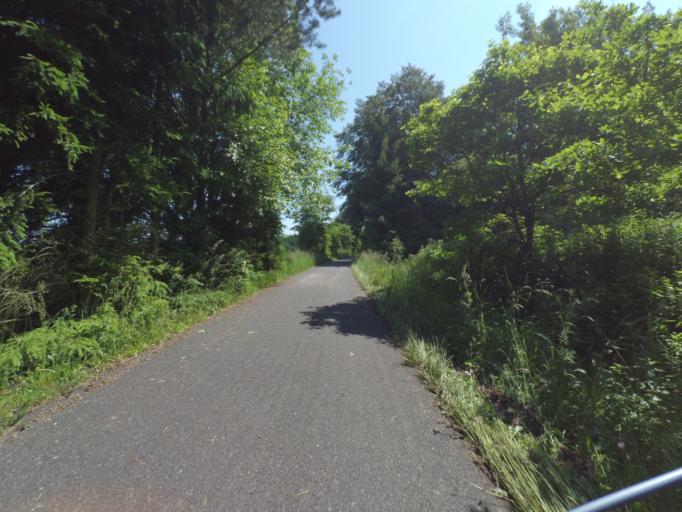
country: DE
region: Rheinland-Pfalz
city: Hollnich
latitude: 50.0715
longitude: 7.4952
